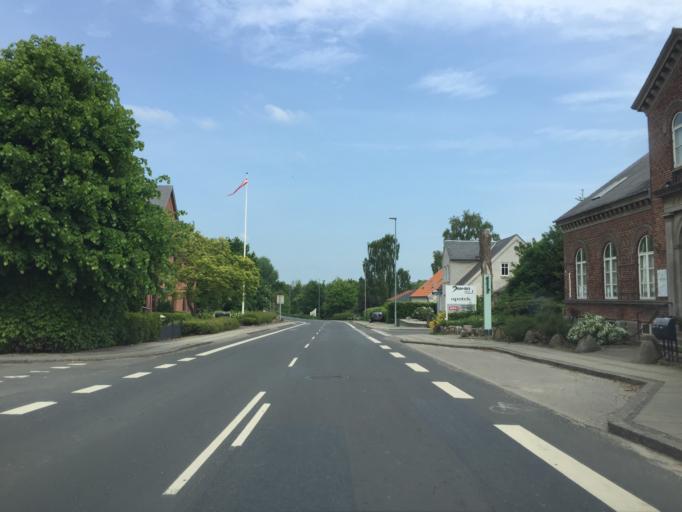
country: DK
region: South Denmark
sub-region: Svendborg Kommune
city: Thuro By
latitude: 55.1707
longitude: 10.7344
